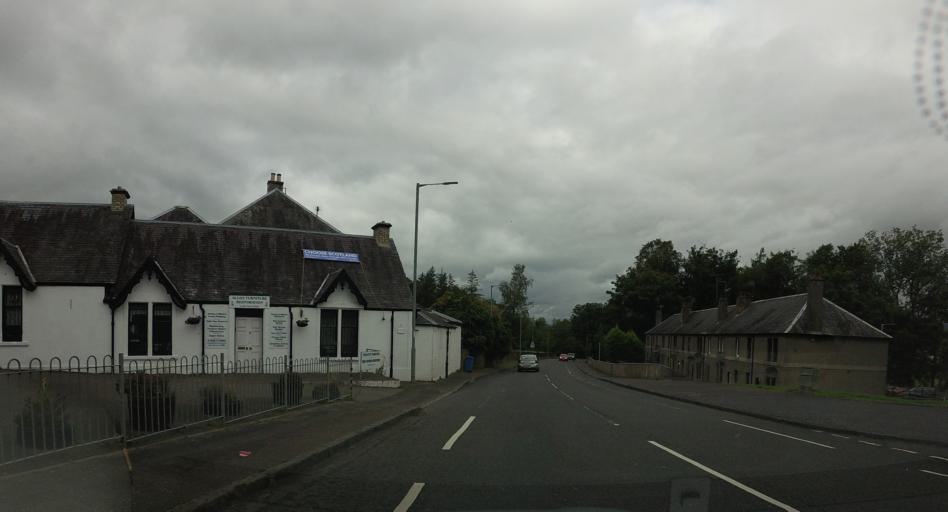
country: GB
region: Scotland
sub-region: Clackmannanshire
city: Clackmannan
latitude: 56.1097
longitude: -3.7545
